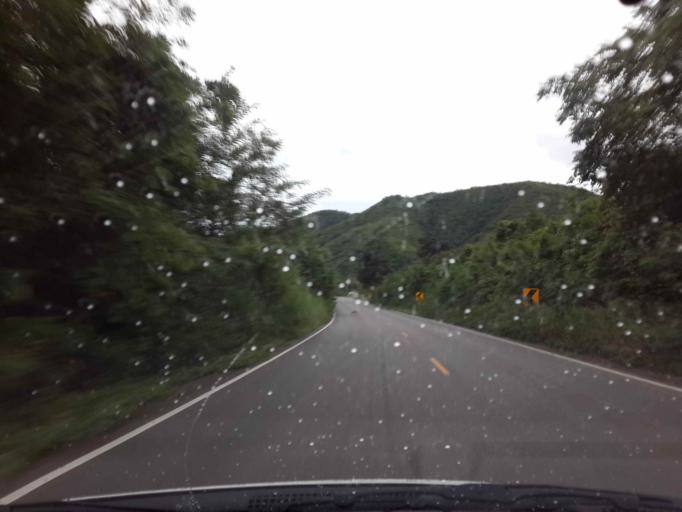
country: TH
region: Ratchaburi
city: Suan Phueng
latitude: 13.5772
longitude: 99.2516
